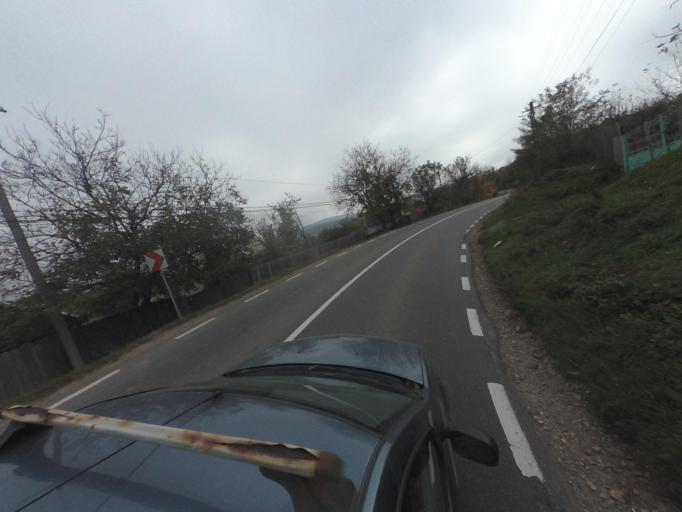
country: RO
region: Vaslui
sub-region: Comuna Bacesti
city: Bacesti
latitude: 46.8288
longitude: 27.2411
